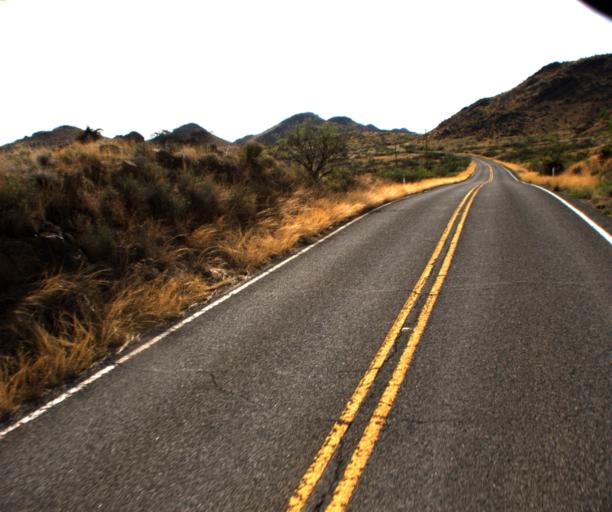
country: US
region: Arizona
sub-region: Cochise County
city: Willcox
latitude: 32.1664
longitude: -109.5805
